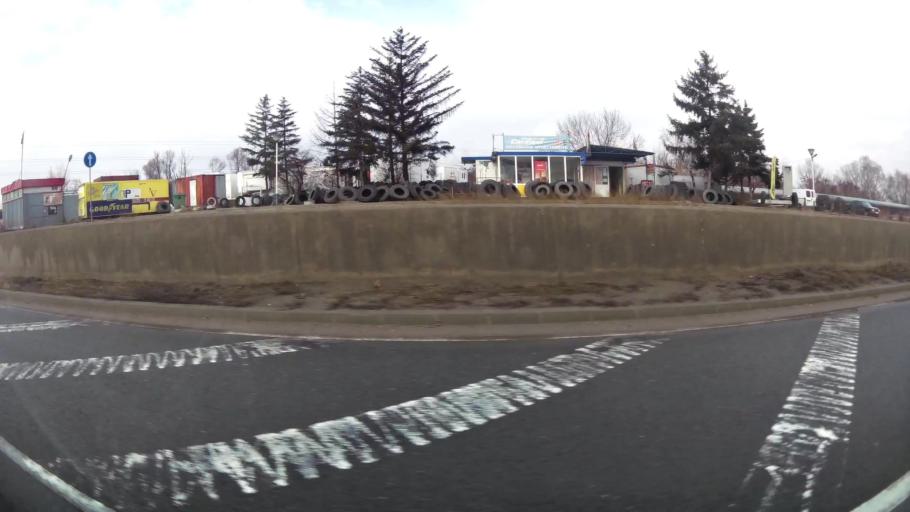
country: BG
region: Sofiya
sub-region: Obshtina Bozhurishte
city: Bozhurishte
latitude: 42.7392
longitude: 23.2510
